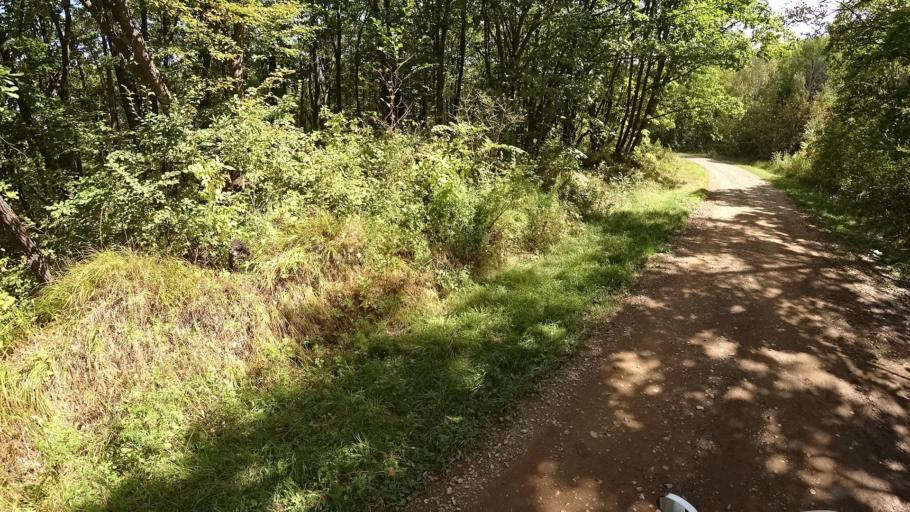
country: RU
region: Primorskiy
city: Kirovskiy
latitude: 44.7600
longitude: 133.6221
